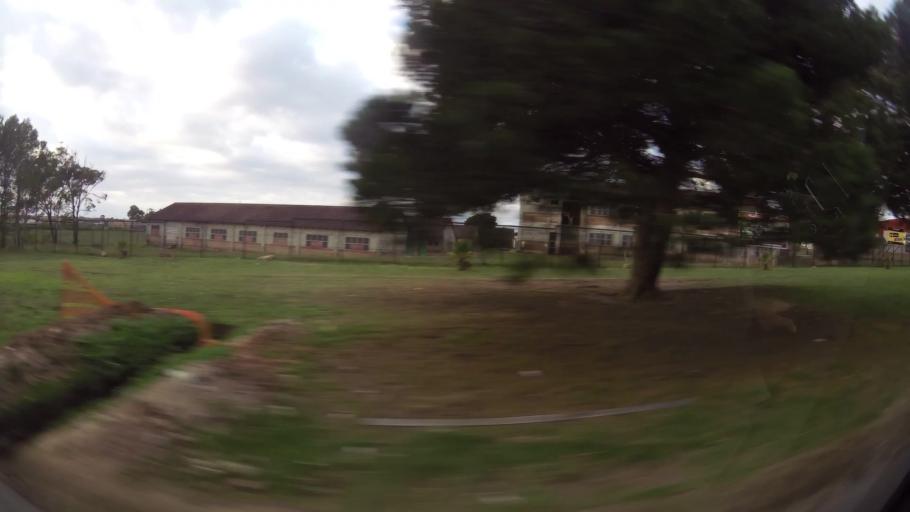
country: ZA
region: Eastern Cape
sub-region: Nelson Mandela Bay Metropolitan Municipality
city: Port Elizabeth
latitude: -33.9837
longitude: 25.5873
